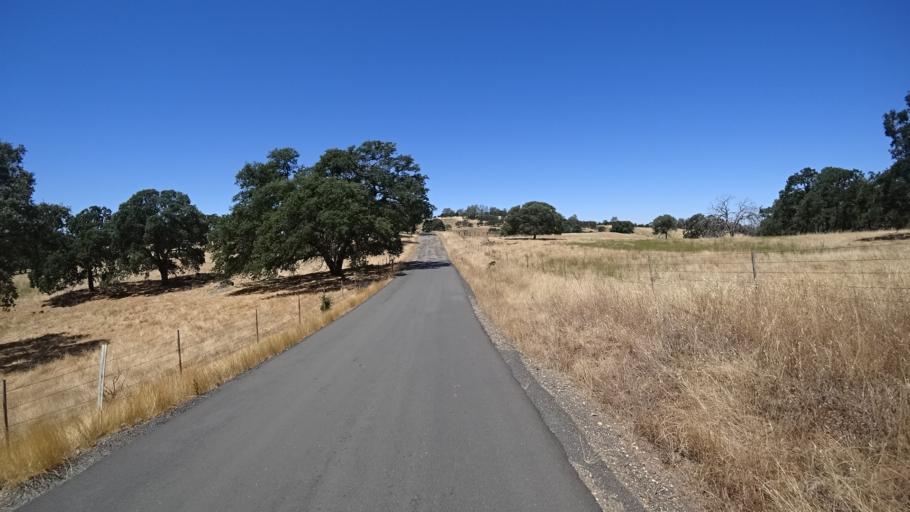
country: US
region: California
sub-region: Calaveras County
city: Rancho Calaveras
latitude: 38.0493
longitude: -120.7963
